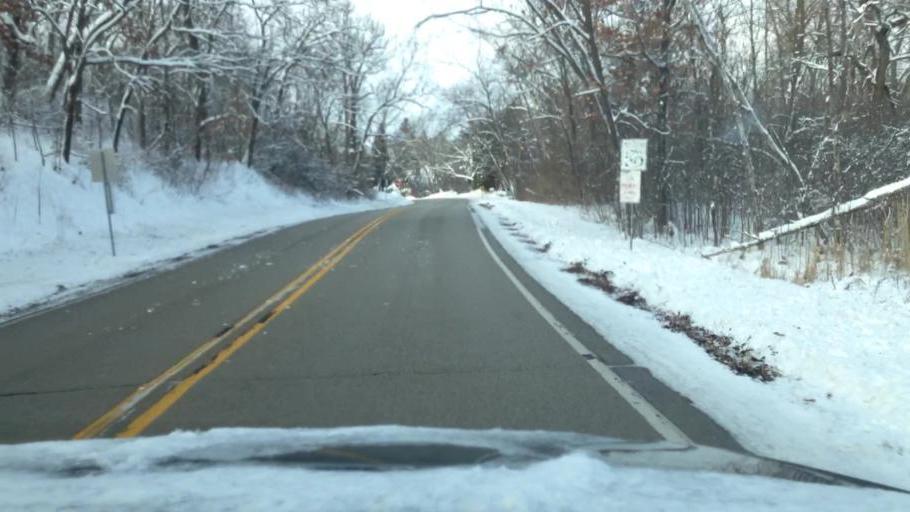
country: US
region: Wisconsin
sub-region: Waukesha County
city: Eagle
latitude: 42.8516
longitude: -88.4337
